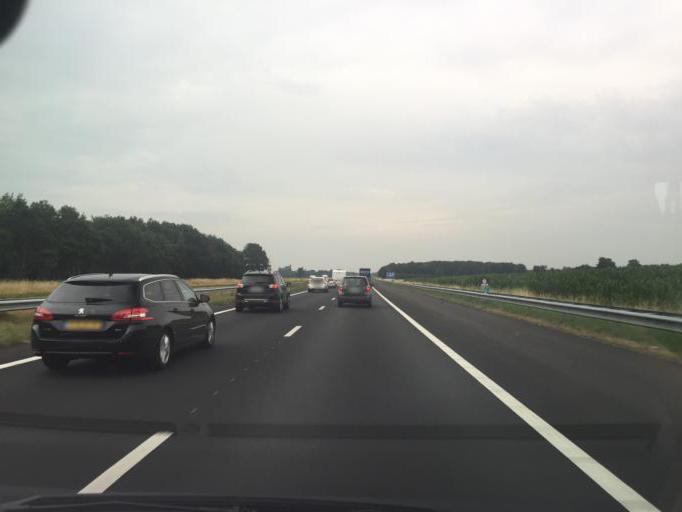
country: NL
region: North Brabant
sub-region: Gemeente Asten
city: Asten
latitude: 51.4121
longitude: 5.7888
